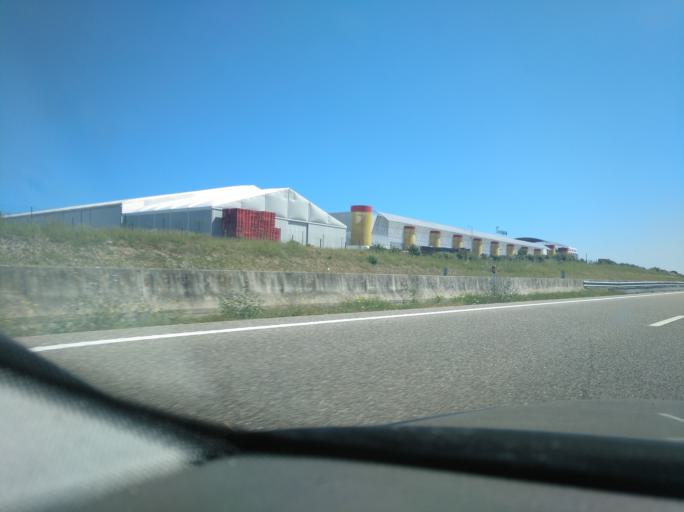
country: PT
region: Santarem
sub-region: Santarem
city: Santarem
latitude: 39.2720
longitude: -8.7132
